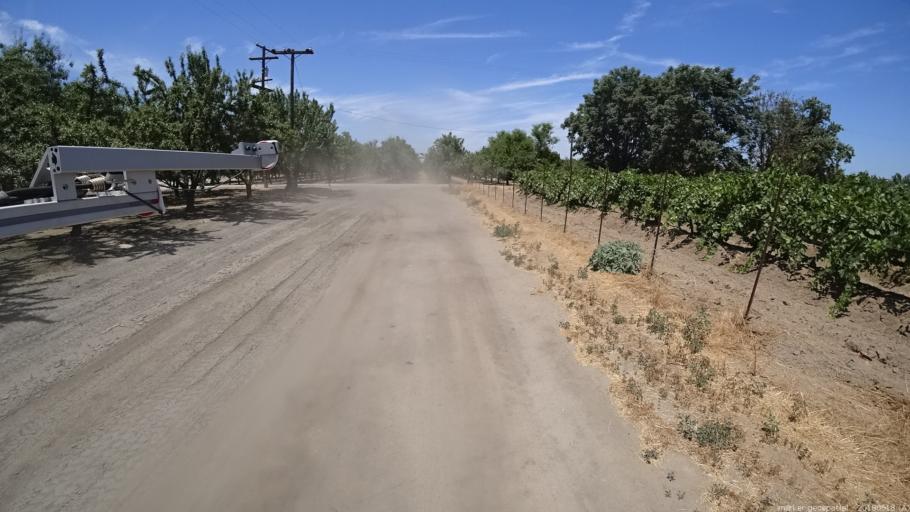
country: US
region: California
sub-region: Madera County
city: Madera
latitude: 36.9057
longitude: -120.1463
